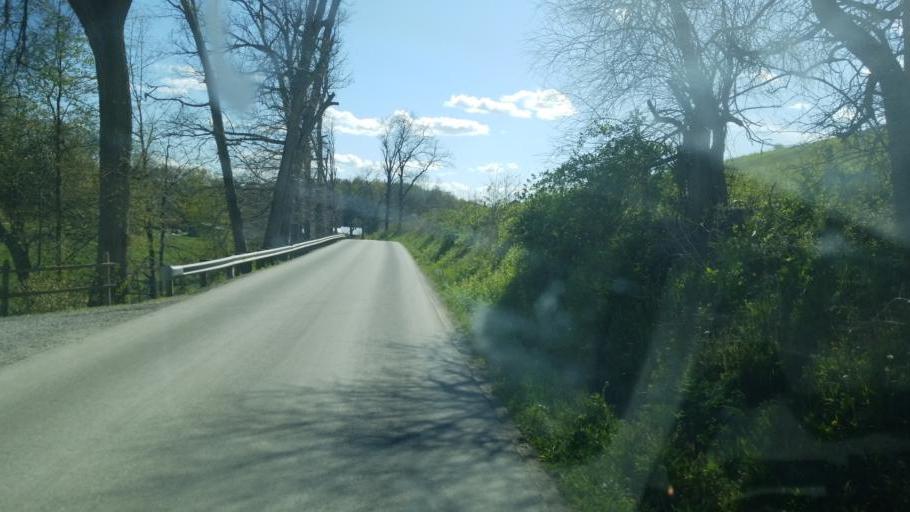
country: US
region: Ohio
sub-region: Holmes County
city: Millersburg
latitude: 40.4416
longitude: -81.8048
